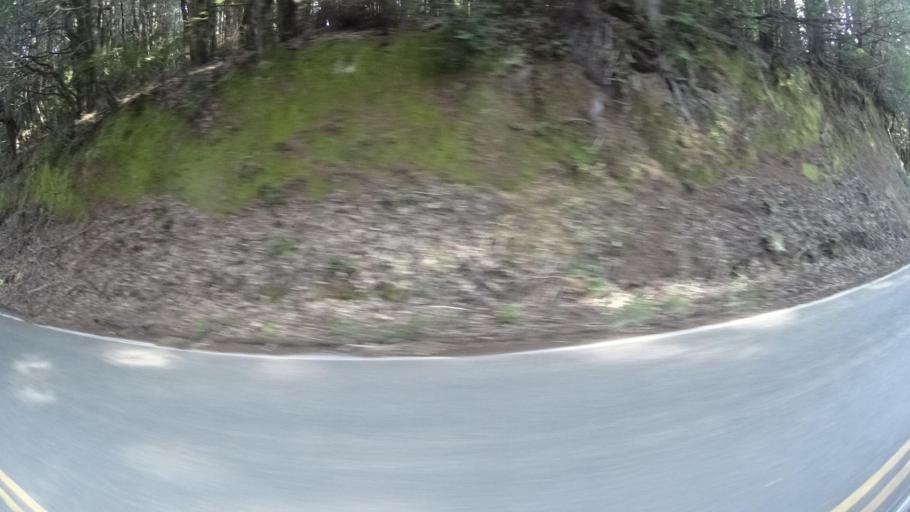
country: US
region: California
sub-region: Humboldt County
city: Bayside
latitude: 40.7503
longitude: -123.9821
